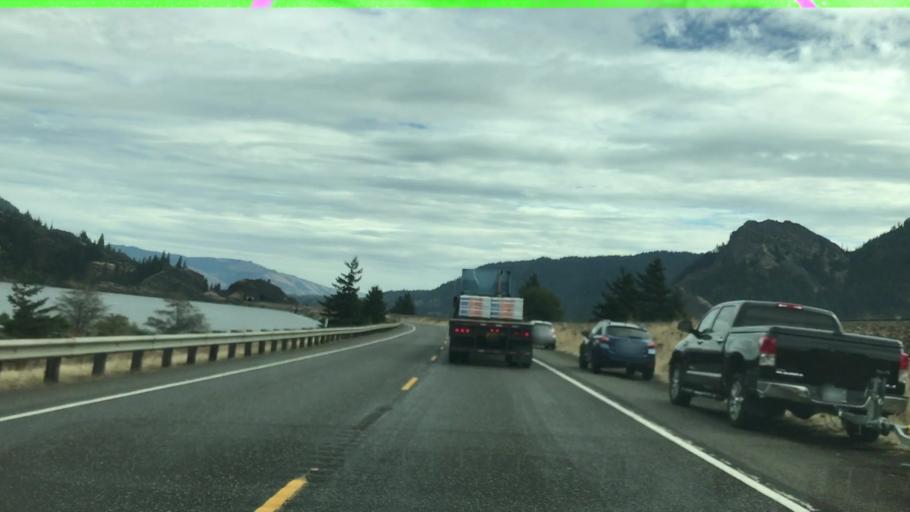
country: US
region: Oregon
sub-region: Hood River County
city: Hood River
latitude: 45.7101
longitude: -121.6400
